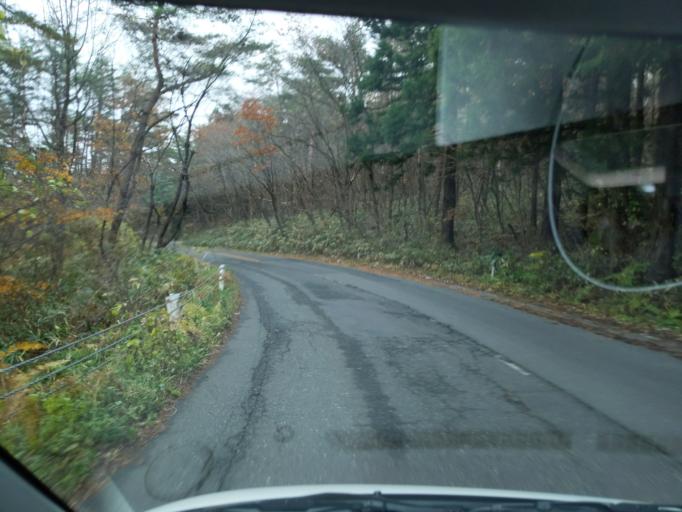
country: JP
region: Iwate
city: Mizusawa
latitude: 39.0429
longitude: 141.0891
